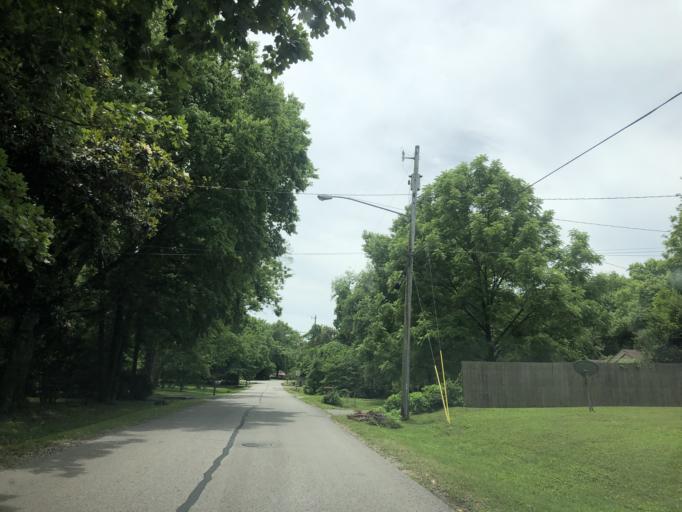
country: US
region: Tennessee
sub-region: Davidson County
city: Oak Hill
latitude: 36.1051
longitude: -86.7851
